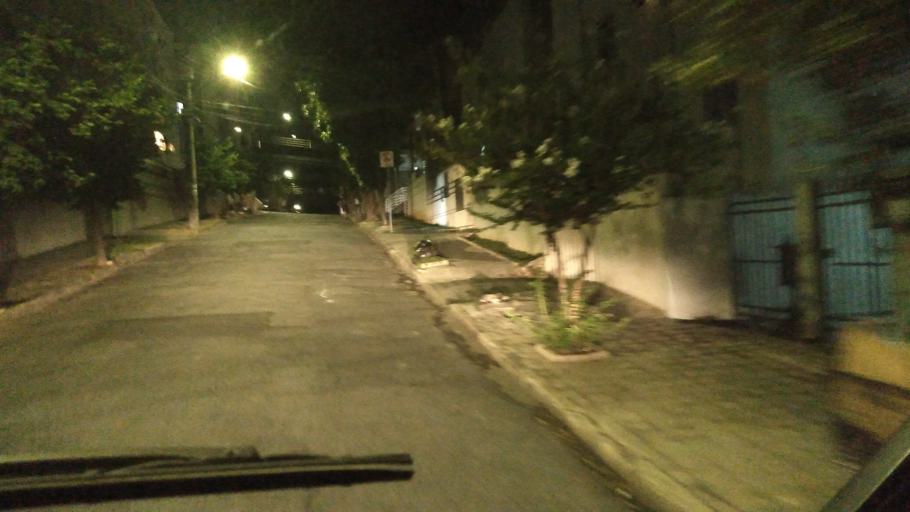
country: BR
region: Minas Gerais
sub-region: Belo Horizonte
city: Belo Horizonte
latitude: -19.8760
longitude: -43.9349
